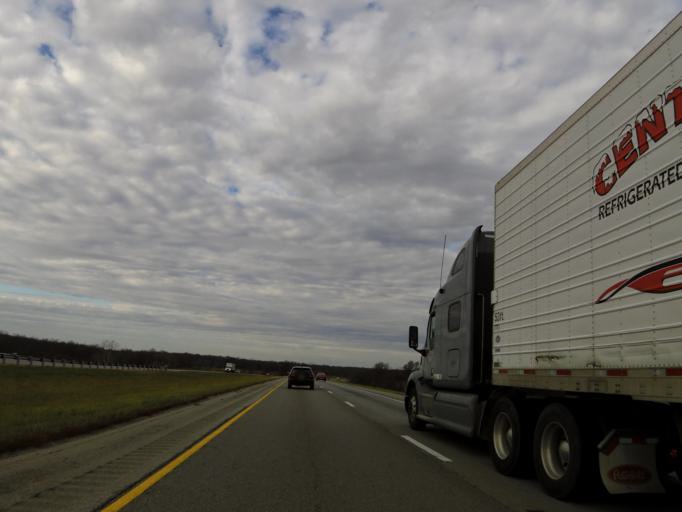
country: US
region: Illinois
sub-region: Clinton County
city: Wamac
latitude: 38.3622
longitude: -89.0723
